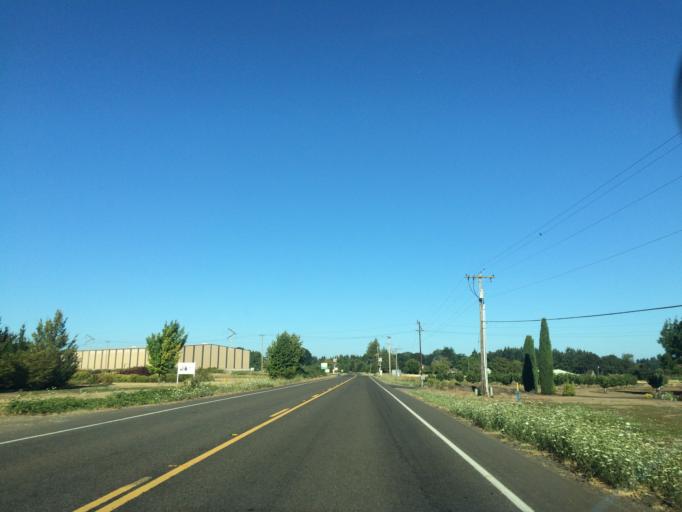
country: US
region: Oregon
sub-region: Marion County
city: Hubbard
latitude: 45.2306
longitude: -122.8335
